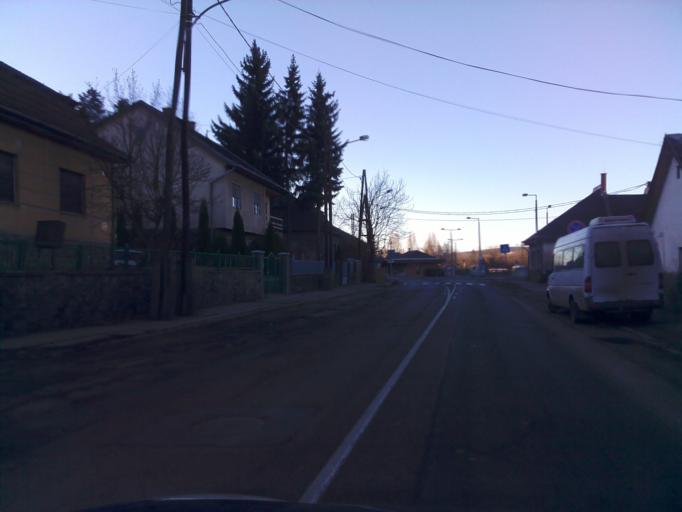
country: HU
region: Nograd
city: Salgotarjan
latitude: 48.0890
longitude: 19.7940
